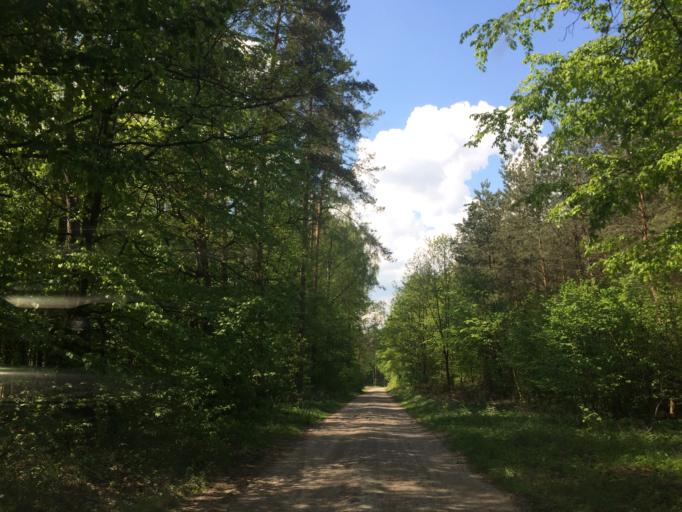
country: PL
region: Warmian-Masurian Voivodeship
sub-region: Powiat nowomiejski
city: Nowe Miasto Lubawskie
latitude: 53.4498
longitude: 19.6268
